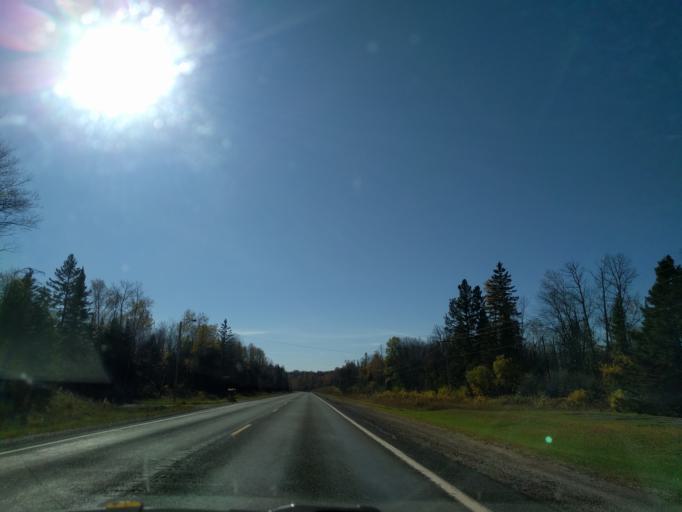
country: US
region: Michigan
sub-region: Marquette County
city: West Ishpeming
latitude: 46.2868
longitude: -88.0114
